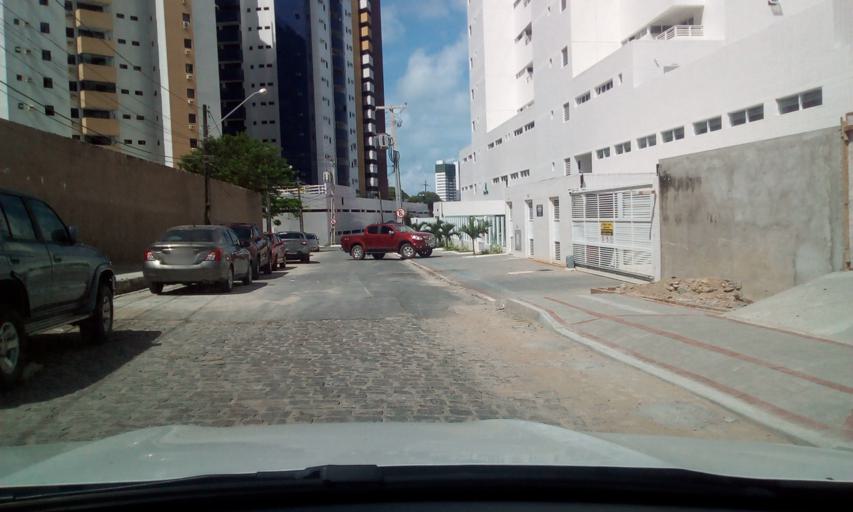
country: BR
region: Paraiba
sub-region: Joao Pessoa
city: Joao Pessoa
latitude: -7.1176
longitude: -34.8349
